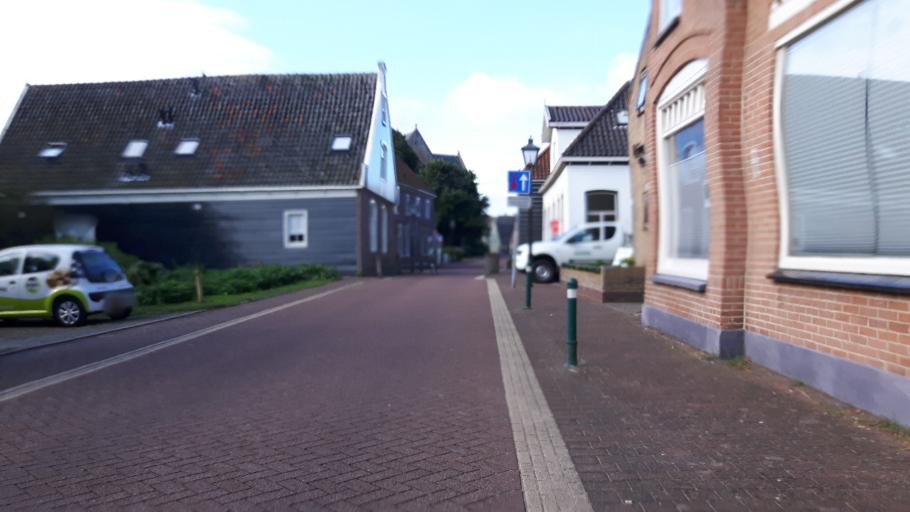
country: NL
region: North Holland
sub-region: Gemeente Purmerend
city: Purmerend
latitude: 52.5718
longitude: 4.9934
